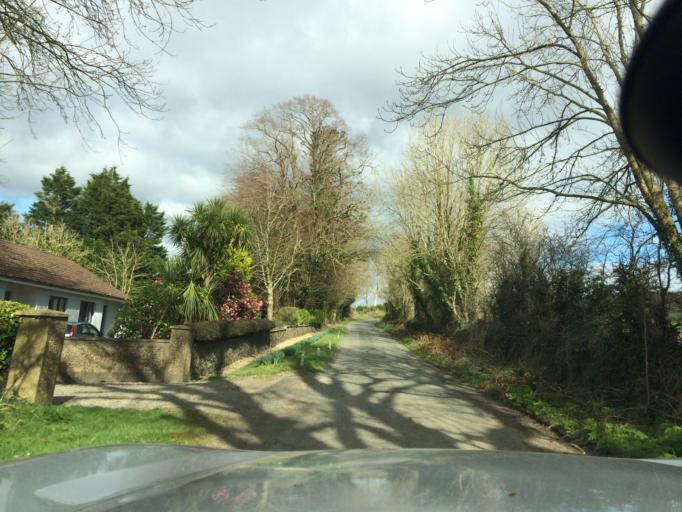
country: IE
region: Munster
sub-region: Waterford
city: Portlaw
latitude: 52.2797
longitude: -7.3560
